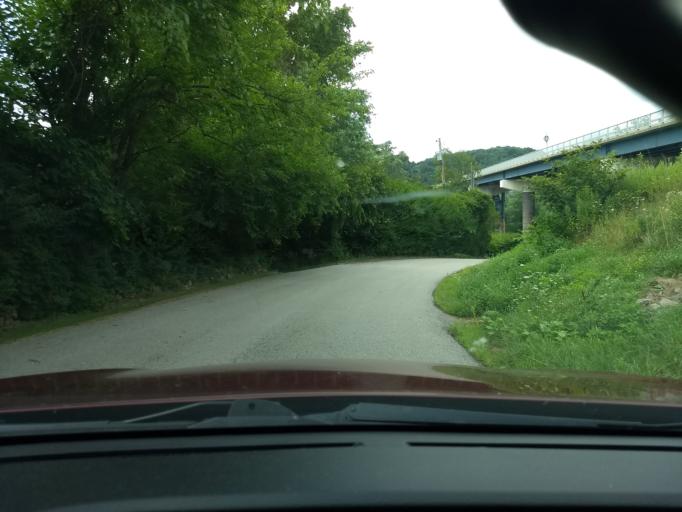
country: US
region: Pennsylvania
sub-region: Armstrong County
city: Freeport
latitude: 40.6656
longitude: -79.6905
